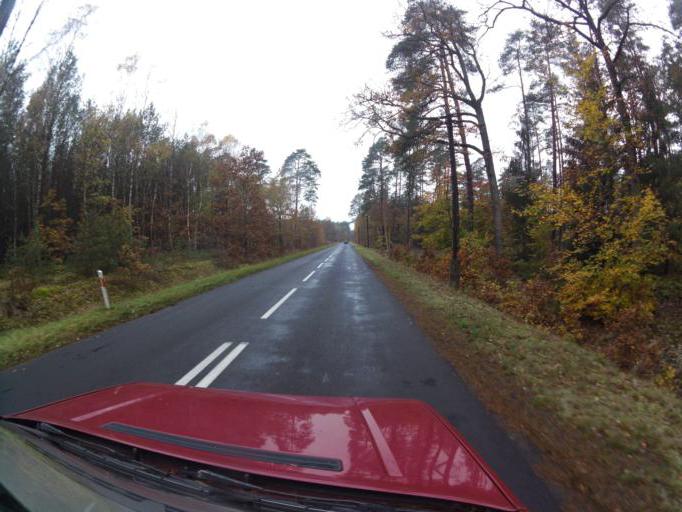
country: PL
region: West Pomeranian Voivodeship
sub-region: Powiat policki
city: Dobra
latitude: 53.5910
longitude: 14.3673
